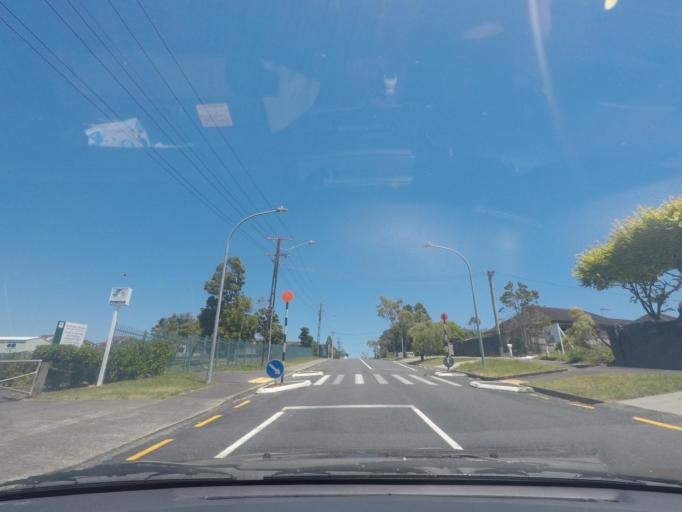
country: NZ
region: Auckland
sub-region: Auckland
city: Waitakere
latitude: -36.9175
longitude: 174.7148
